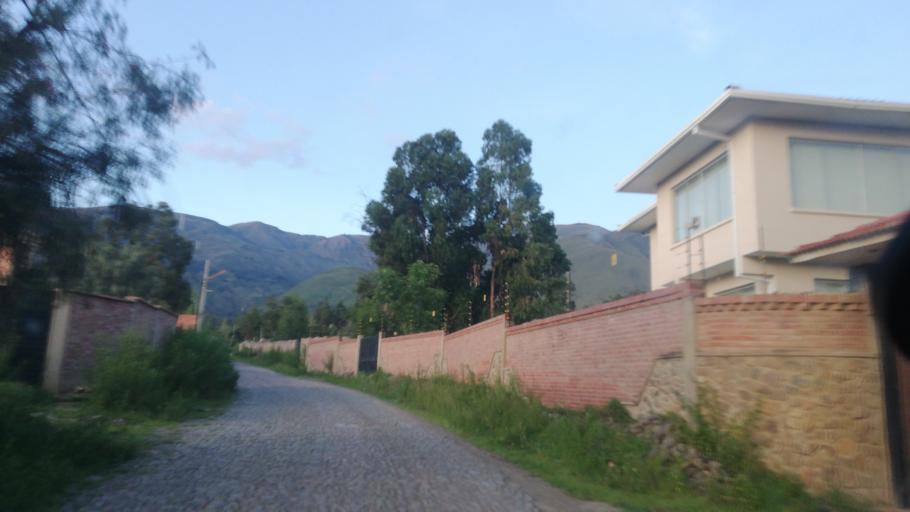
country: BO
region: Cochabamba
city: Cochabamba
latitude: -17.3373
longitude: -66.2099
